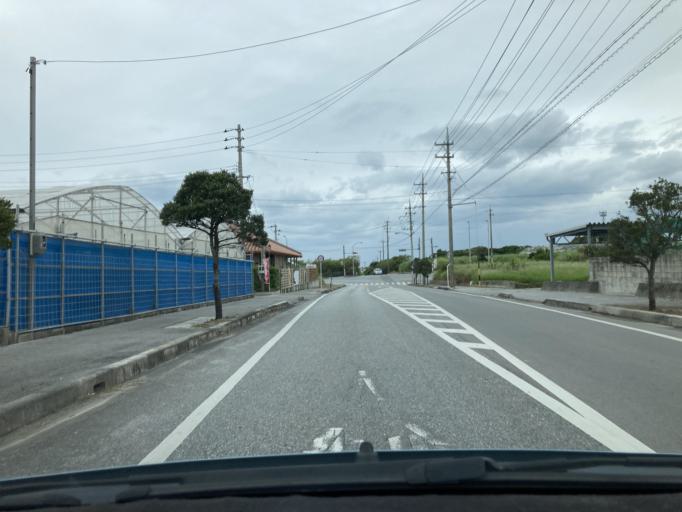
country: JP
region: Okinawa
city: Tomigusuku
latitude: 26.1606
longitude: 127.7038
